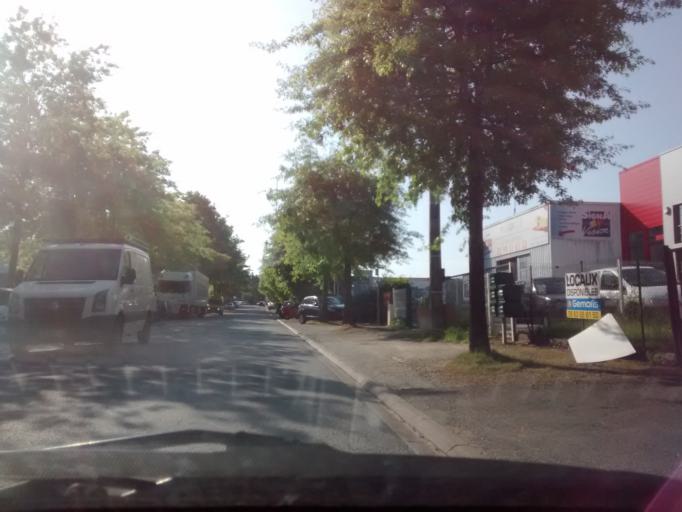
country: FR
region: Brittany
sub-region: Departement d'Ille-et-Vilaine
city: Chantepie
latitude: 48.1035
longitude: -1.6251
